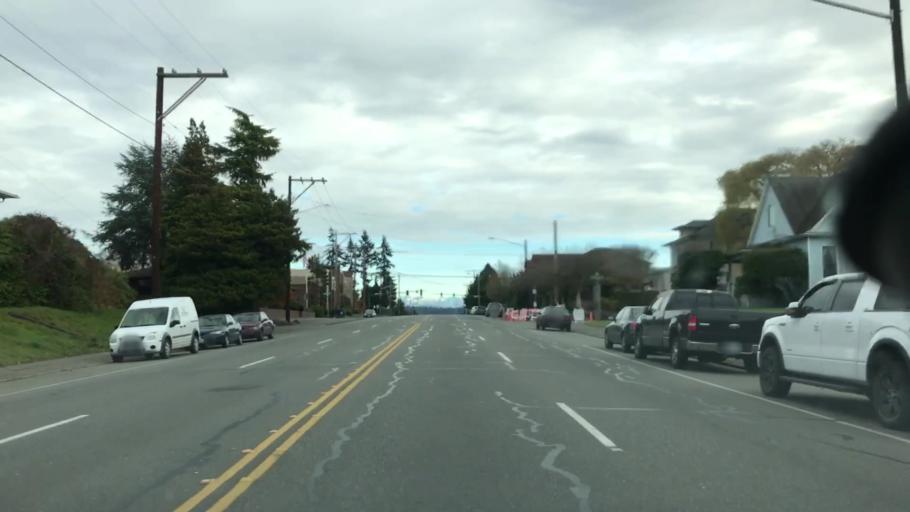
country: US
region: Washington
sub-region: Snohomish County
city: Everett
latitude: 47.9818
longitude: -122.1966
